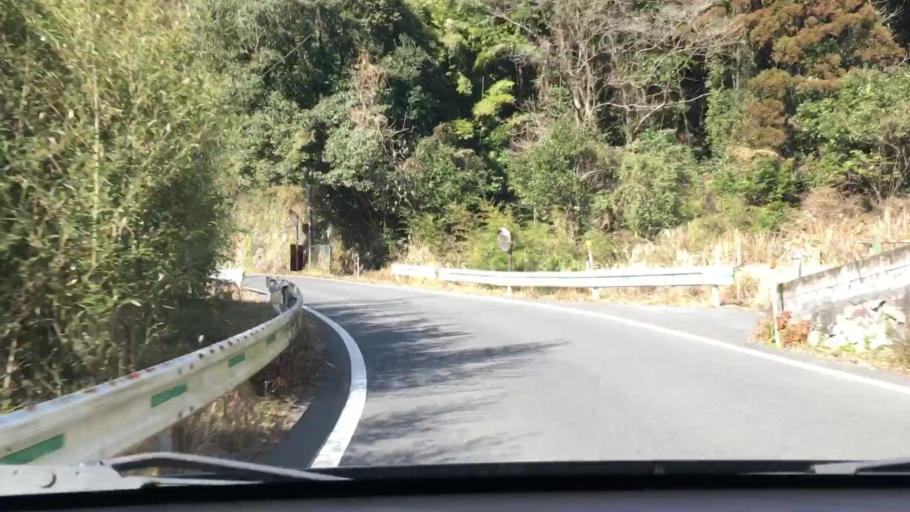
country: JP
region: Kagoshima
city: Ijuin
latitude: 31.7132
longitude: 130.4169
